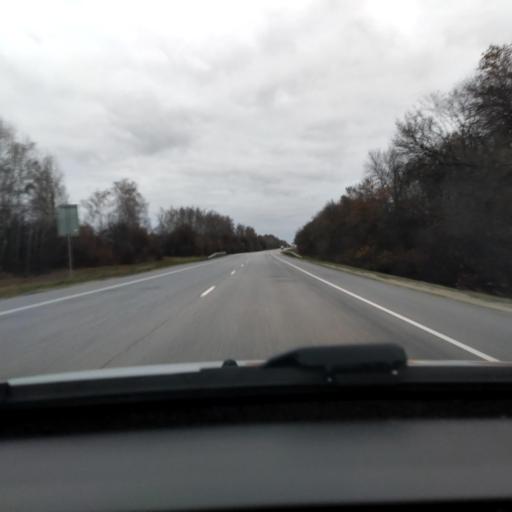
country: RU
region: Lipetsk
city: Borinskoye
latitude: 52.3683
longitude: 39.2069
